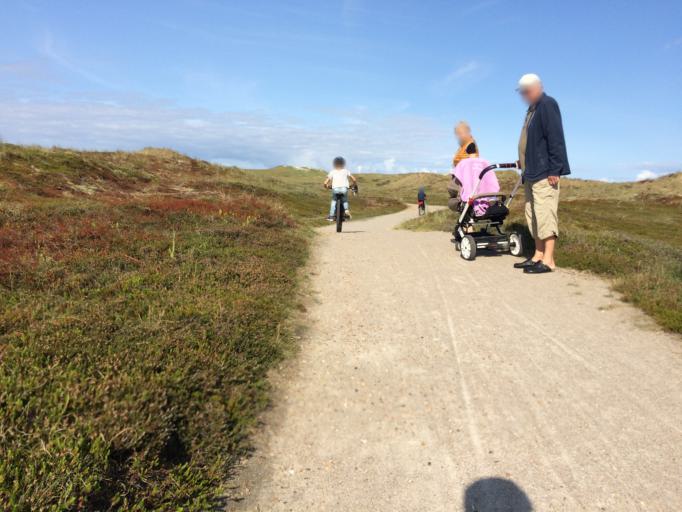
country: DK
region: Central Jutland
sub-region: Ringkobing-Skjern Kommune
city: Hvide Sande
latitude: 55.9206
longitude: 8.1571
